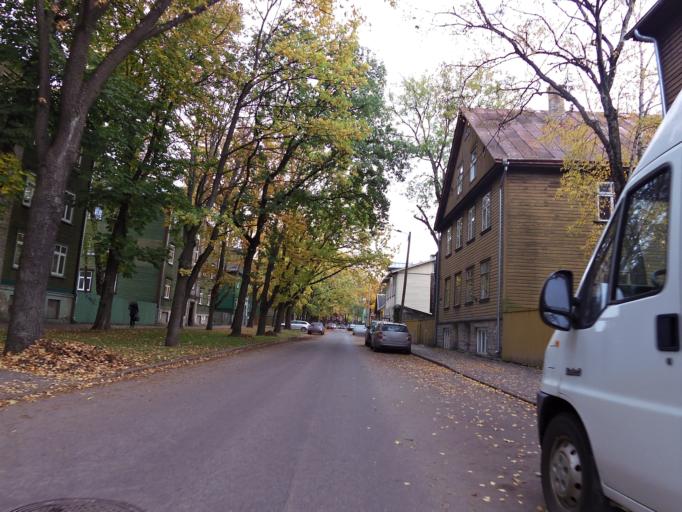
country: EE
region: Harju
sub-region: Tallinna linn
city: Tallinn
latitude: 59.4391
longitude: 24.7218
